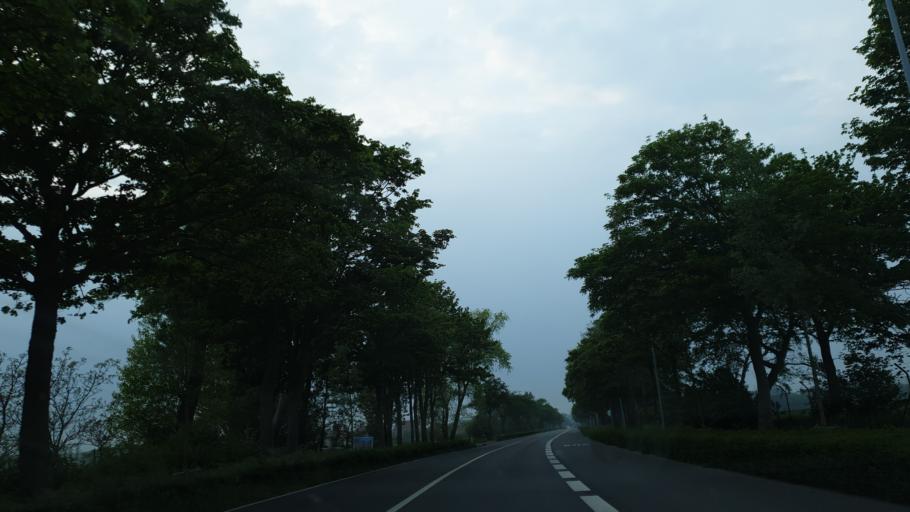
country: BE
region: Flanders
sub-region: Provincie West-Vlaanderen
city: Koksijde
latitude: 51.0865
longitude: 2.6390
